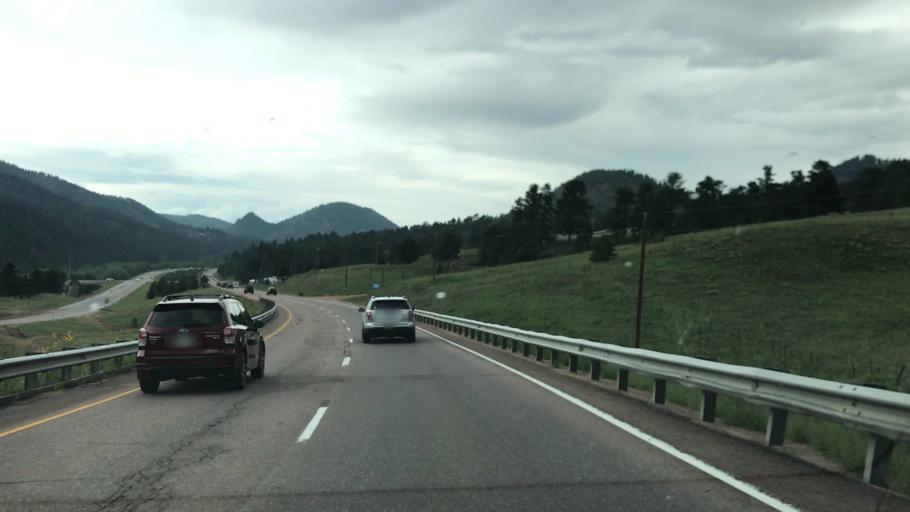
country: US
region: Colorado
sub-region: El Paso County
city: Cascade-Chipita Park
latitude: 38.9384
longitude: -105.0105
